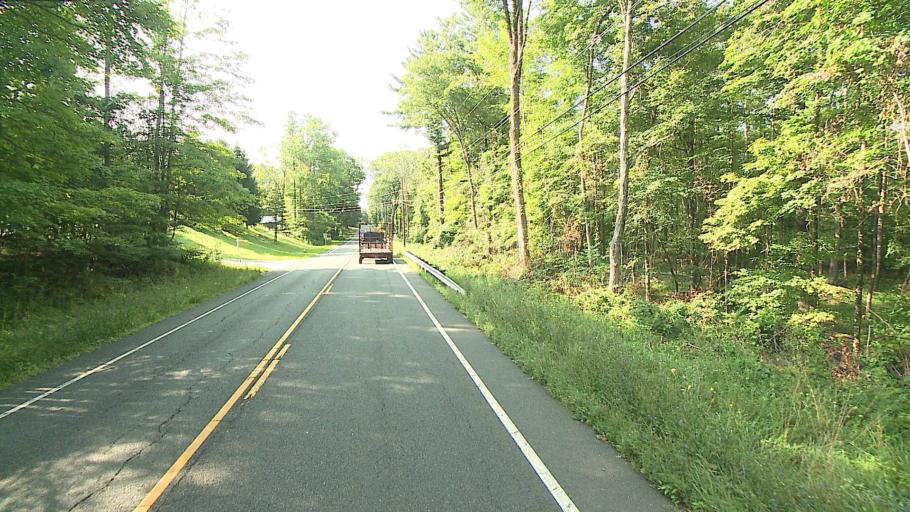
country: US
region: Connecticut
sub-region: Litchfield County
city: Canaan
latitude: 41.9483
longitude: -73.3598
